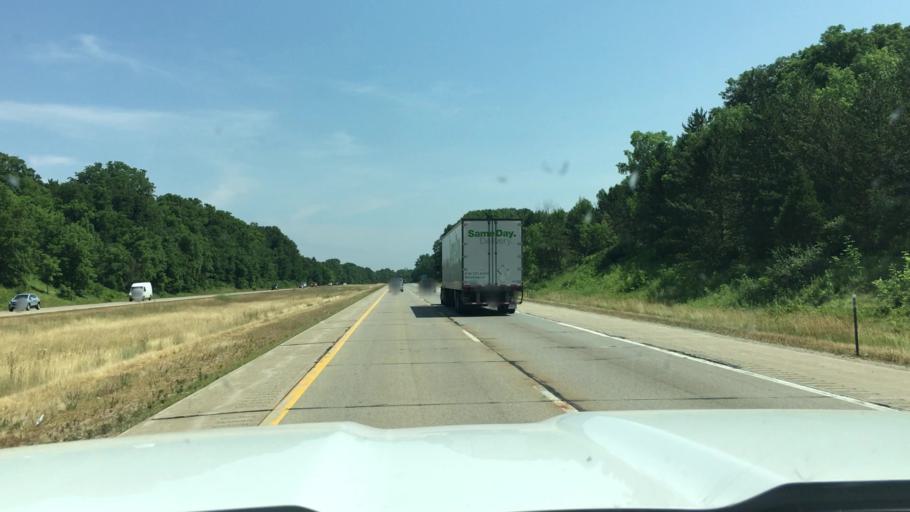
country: US
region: Michigan
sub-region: Eaton County
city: Waverly
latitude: 42.8011
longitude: -84.6370
